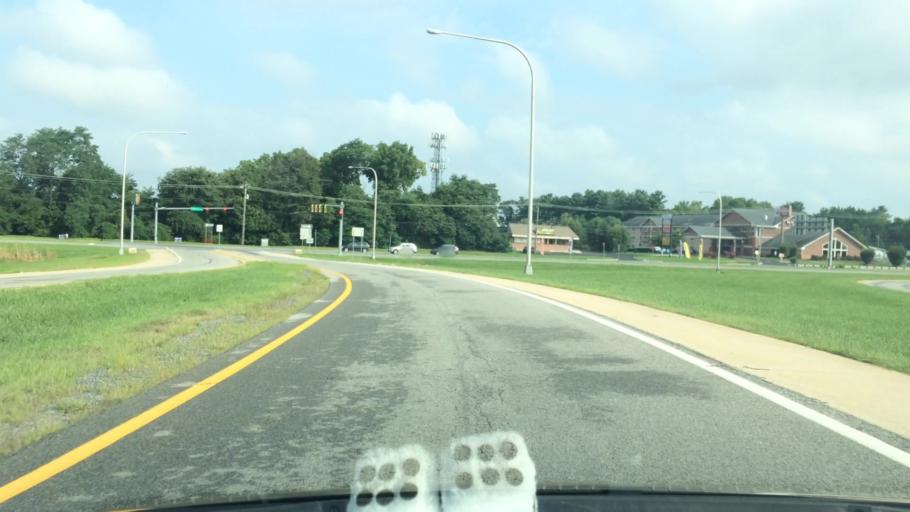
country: US
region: Delaware
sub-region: New Castle County
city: Bear
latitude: 39.6368
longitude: -75.6508
